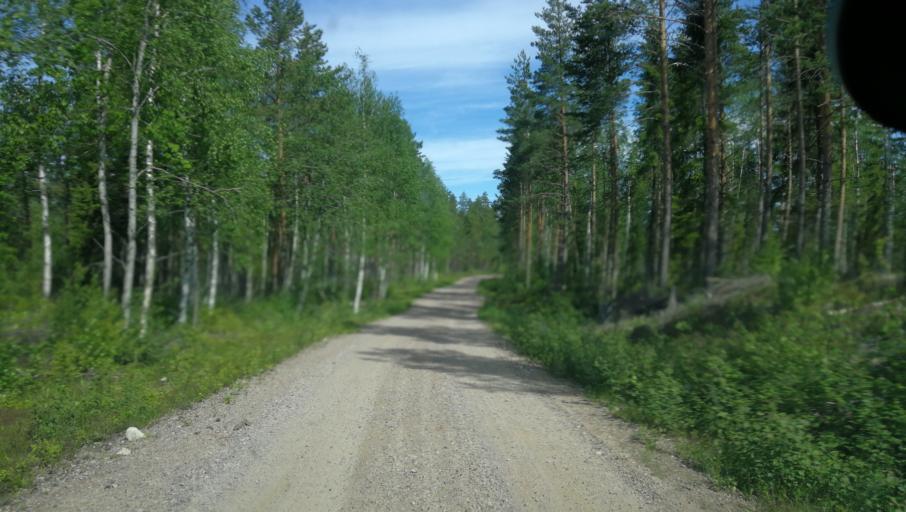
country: SE
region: Dalarna
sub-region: Vansbro Kommun
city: Vansbro
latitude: 60.8303
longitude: 14.1607
